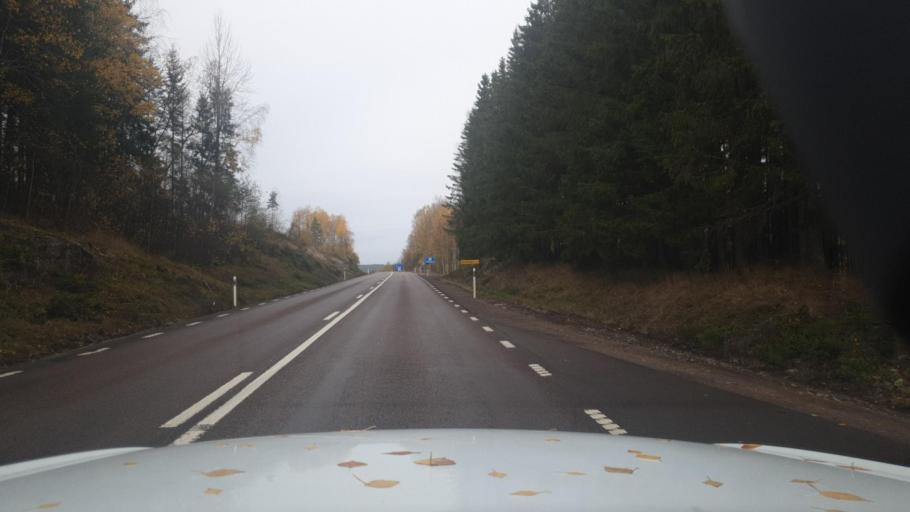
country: SE
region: Vaermland
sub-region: Karlstads Kommun
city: Edsvalla
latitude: 59.5477
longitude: 13.0623
